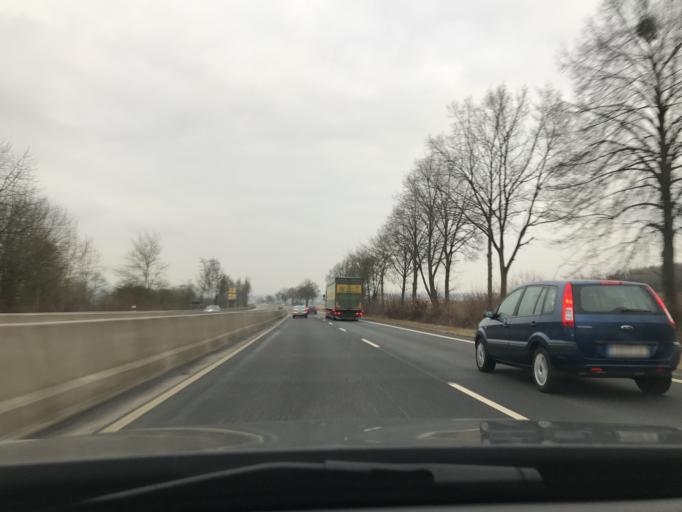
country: DE
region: Hesse
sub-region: Regierungsbezirk Kassel
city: Espenau
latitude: 51.3775
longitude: 9.4427
